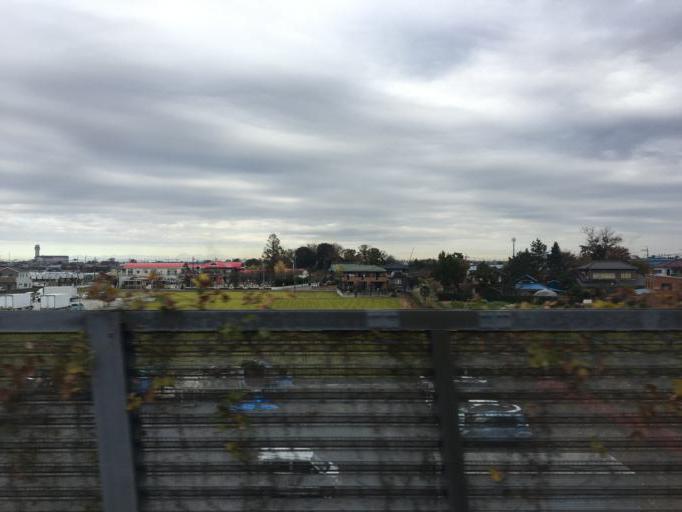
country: JP
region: Saitama
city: Yoshikawa
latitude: 35.8766
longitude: 139.8351
